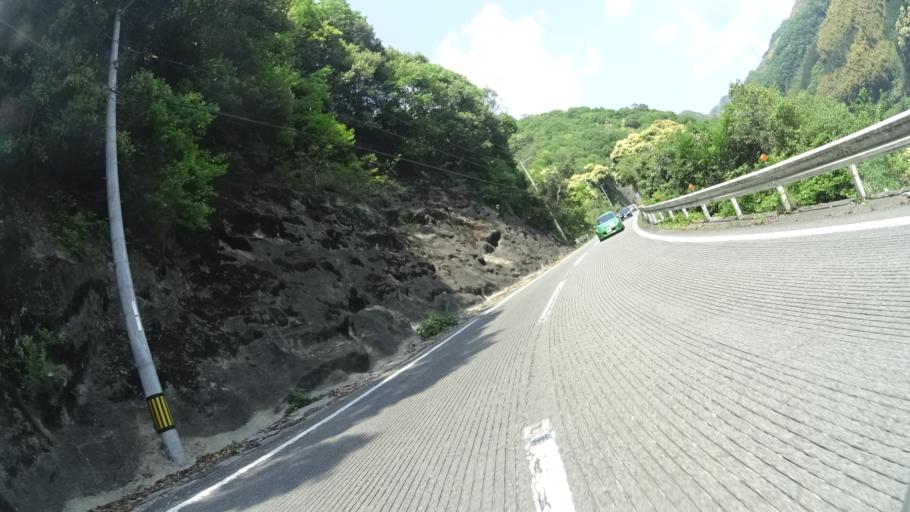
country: JP
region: Ehime
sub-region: Shikoku-chuo Shi
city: Matsuyama
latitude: 33.8745
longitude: 132.8322
